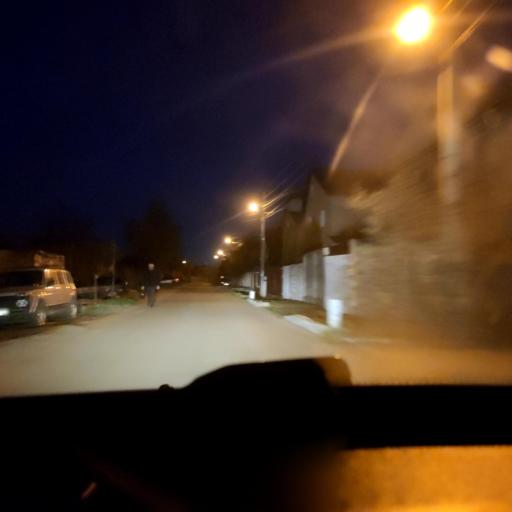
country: RU
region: Voronezj
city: Voronezh
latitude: 51.7430
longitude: 39.2609
